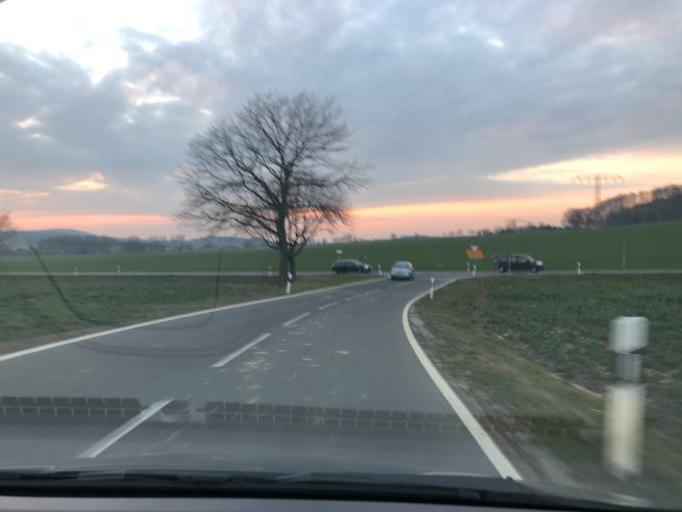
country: DE
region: Saxony
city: Haselbachtal
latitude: 51.2401
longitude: 14.0602
